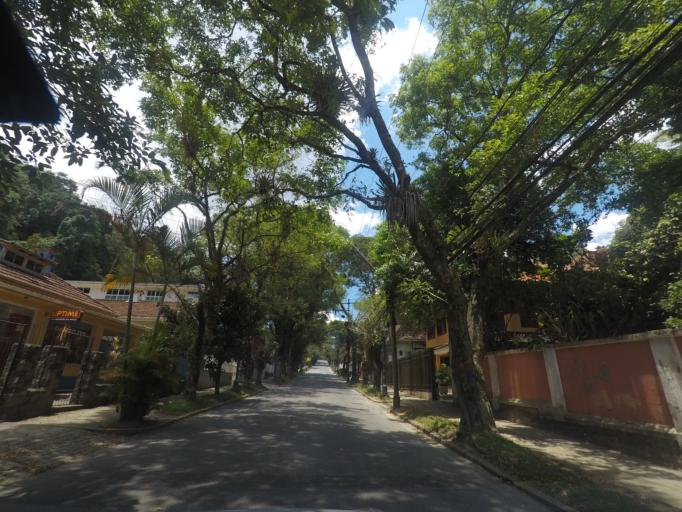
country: BR
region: Rio de Janeiro
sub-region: Petropolis
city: Petropolis
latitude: -22.5073
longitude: -43.1739
